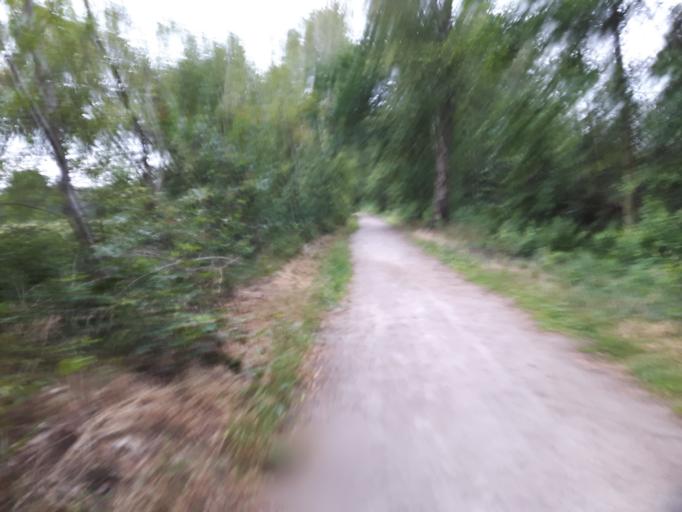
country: DE
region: Lower Saxony
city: Stelle
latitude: 53.4210
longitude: 10.0493
